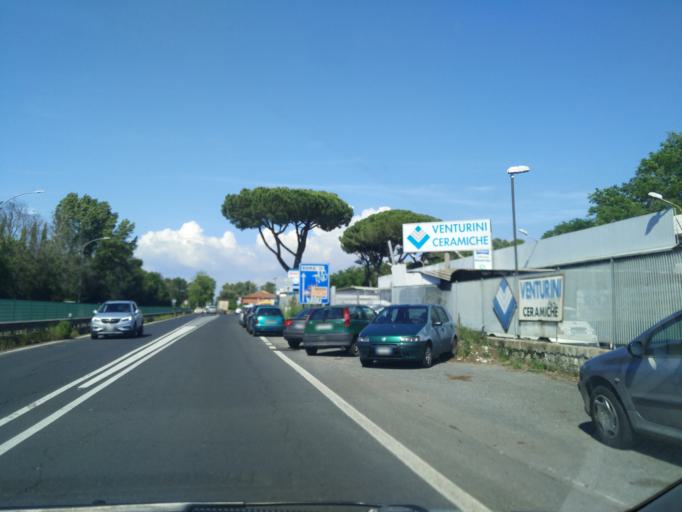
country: IT
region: Latium
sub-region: Citta metropolitana di Roma Capitale
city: Vitinia
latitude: 41.8224
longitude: 12.4400
